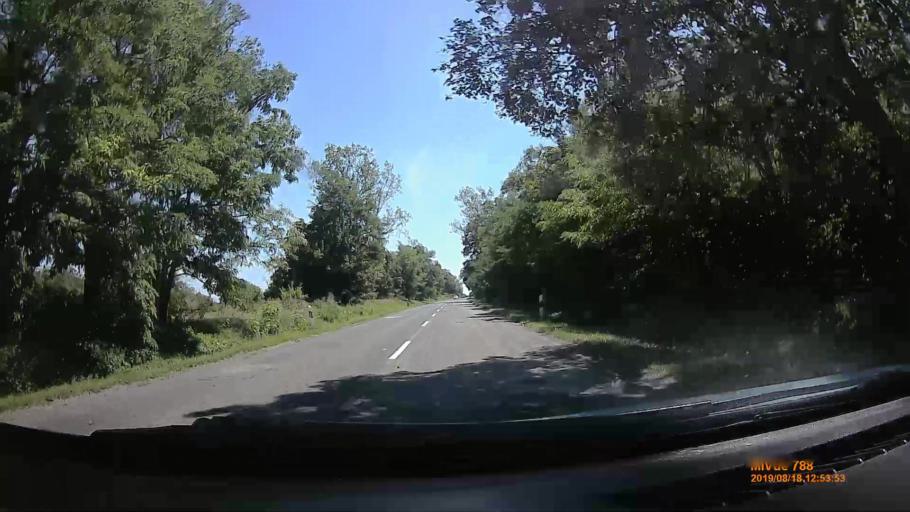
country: HU
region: Fejer
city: Aba
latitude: 47.0466
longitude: 18.5274
